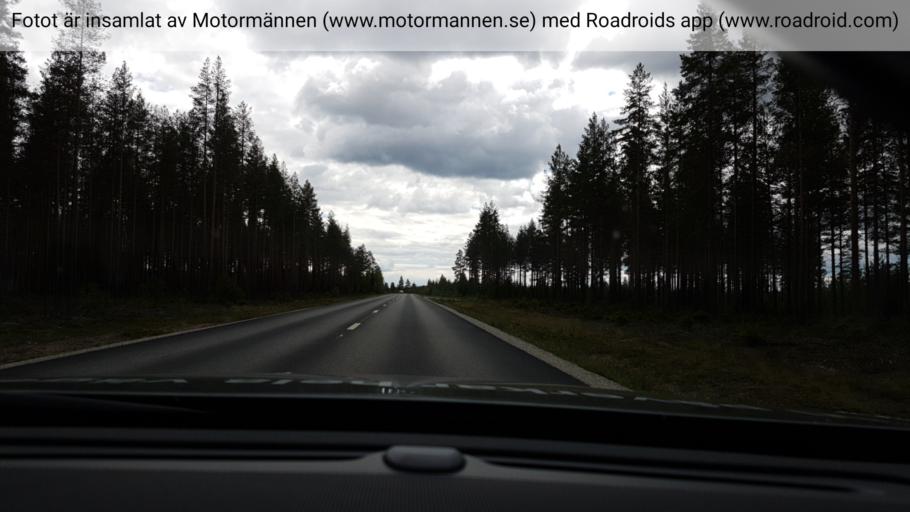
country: SE
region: Vaesterbotten
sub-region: Vindelns Kommun
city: Vindeln
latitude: 64.0765
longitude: 19.6337
